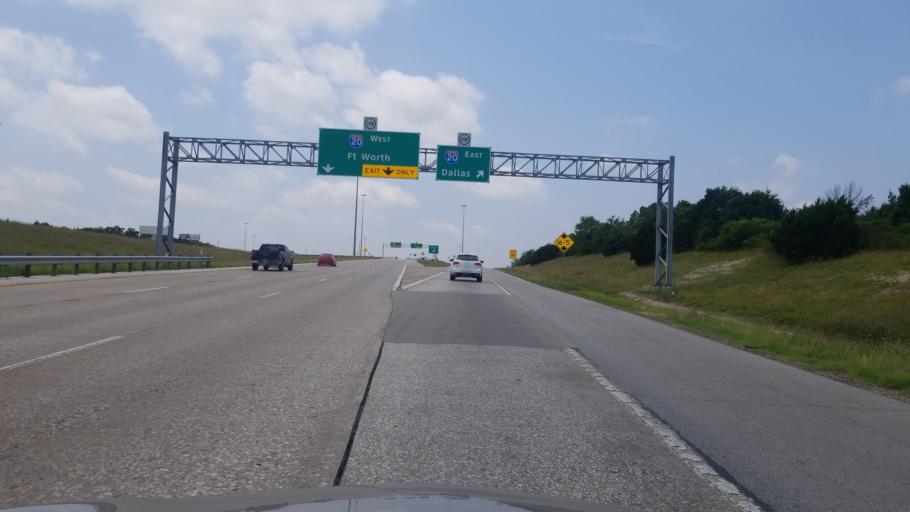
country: US
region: Texas
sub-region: Dallas County
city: Duncanville
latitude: 32.6787
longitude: -96.9461
